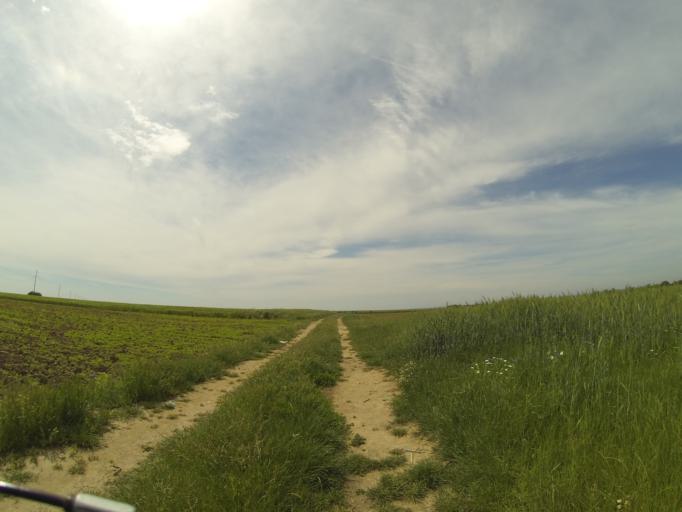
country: RO
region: Dolj
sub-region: Comuna Ghindeni
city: Ghindeni
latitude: 44.2135
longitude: 23.9388
